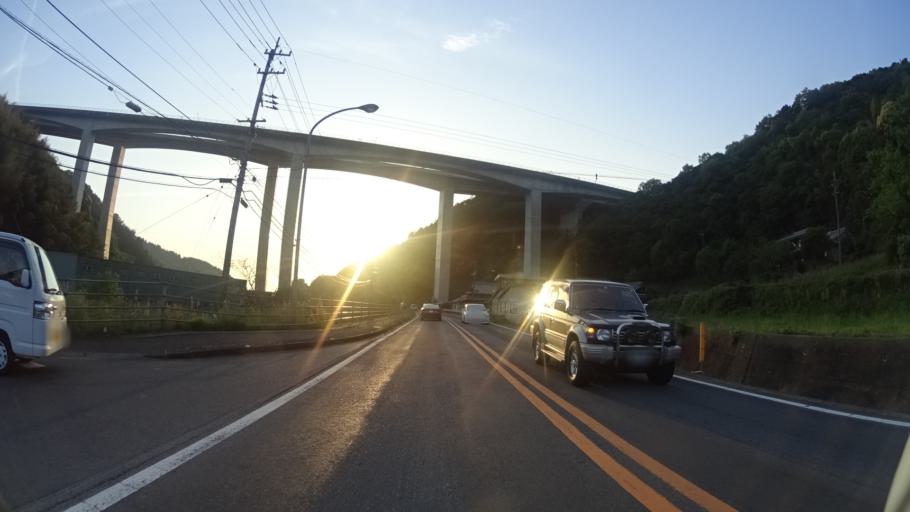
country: JP
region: Ehime
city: Kawanoecho
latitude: 33.9922
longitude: 133.6217
